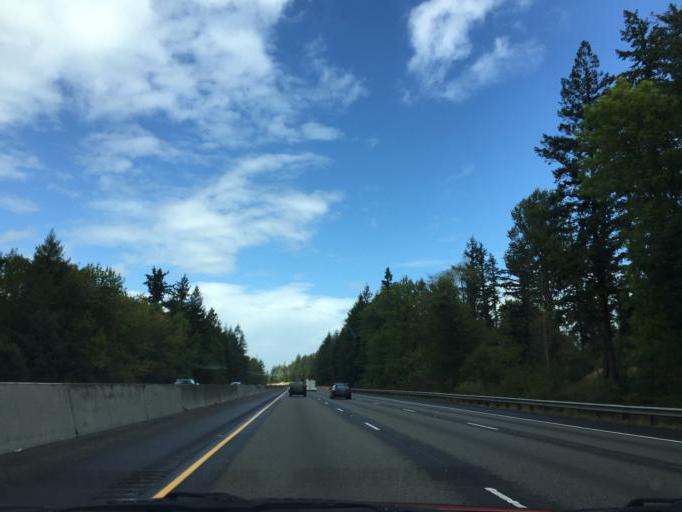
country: US
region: Washington
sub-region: Thurston County
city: Grand Mound
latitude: 46.8541
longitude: -122.9762
